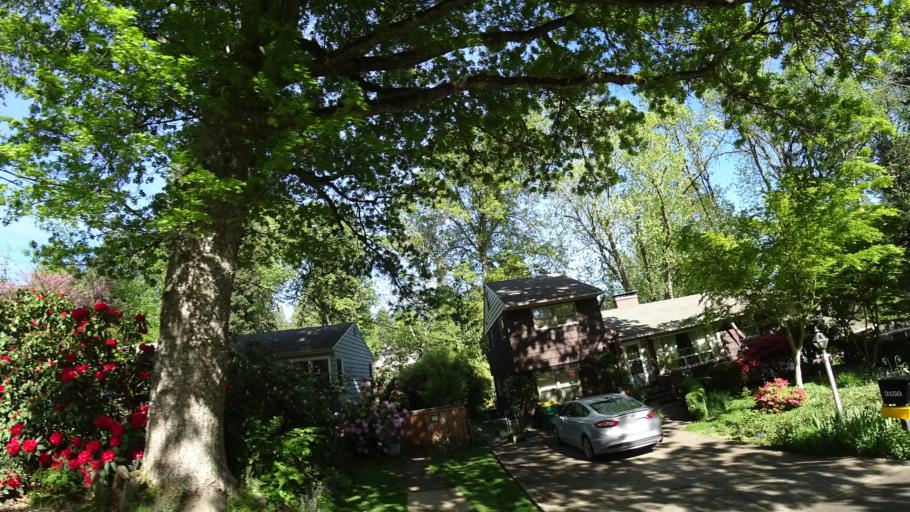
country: US
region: Oregon
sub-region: Washington County
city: West Slope
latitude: 45.4972
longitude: -122.7535
